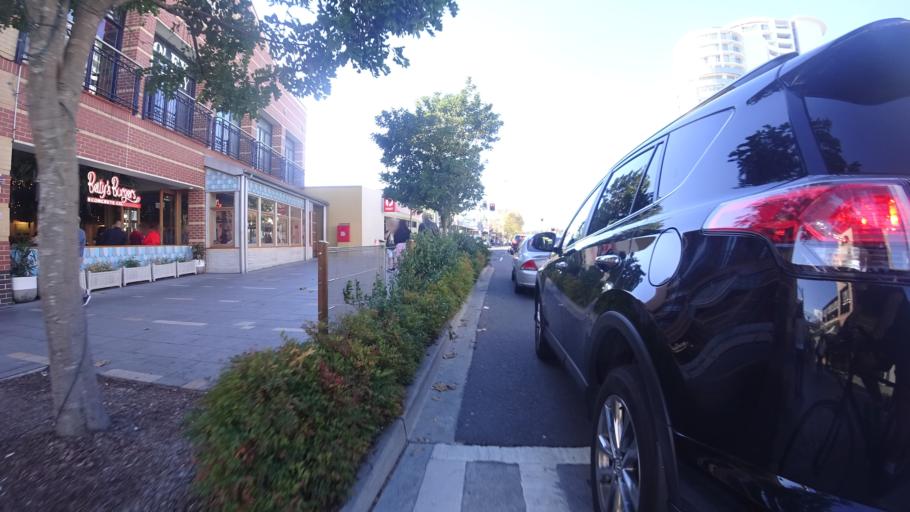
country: AU
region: New South Wales
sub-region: The Hills Shire
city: Castle Hill
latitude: -33.7325
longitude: 151.0053
